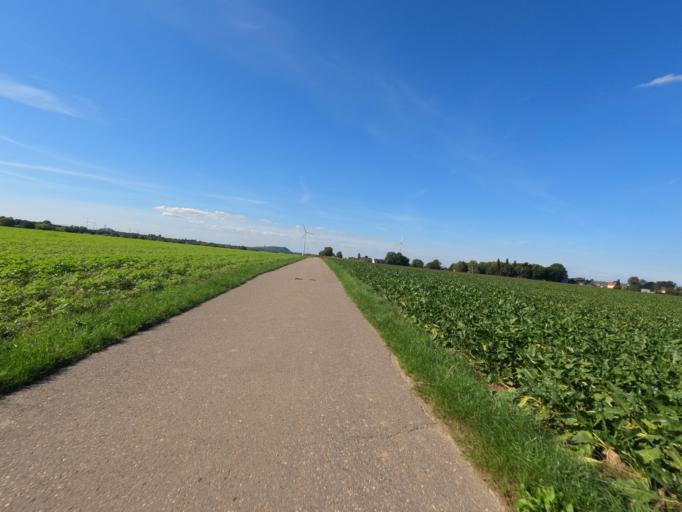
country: DE
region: North Rhine-Westphalia
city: Siersdorf
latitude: 50.8900
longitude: 6.2235
